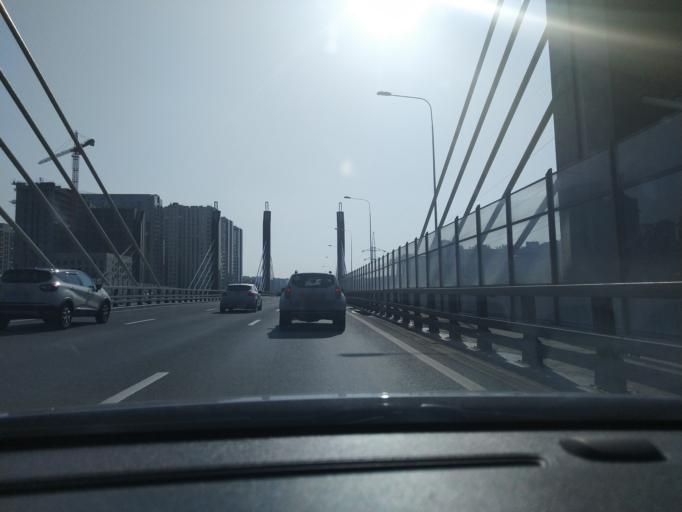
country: RU
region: St.-Petersburg
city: Kupchino
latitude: 59.8302
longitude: 30.3212
